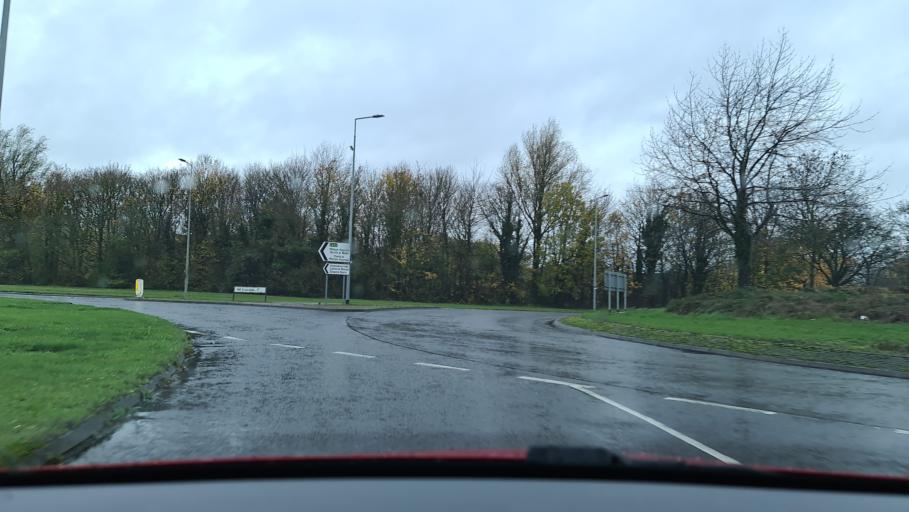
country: GB
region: England
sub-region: Milton Keynes
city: Milton Keynes
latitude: 52.0582
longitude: -0.7447
